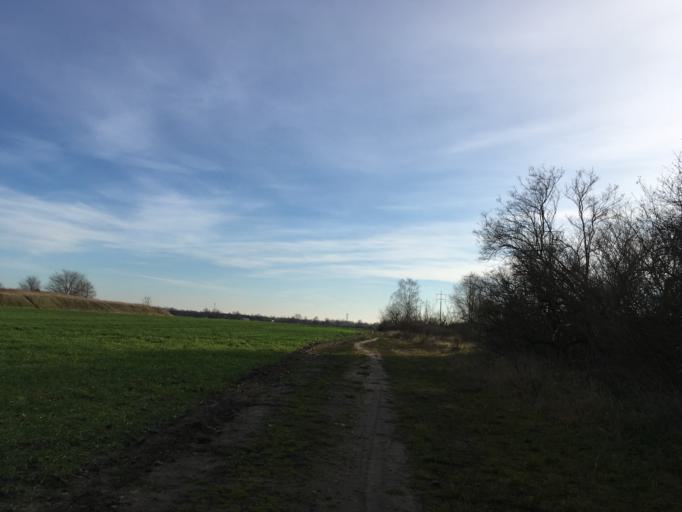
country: DE
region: Berlin
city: Buchholz
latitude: 52.6240
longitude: 13.4377
